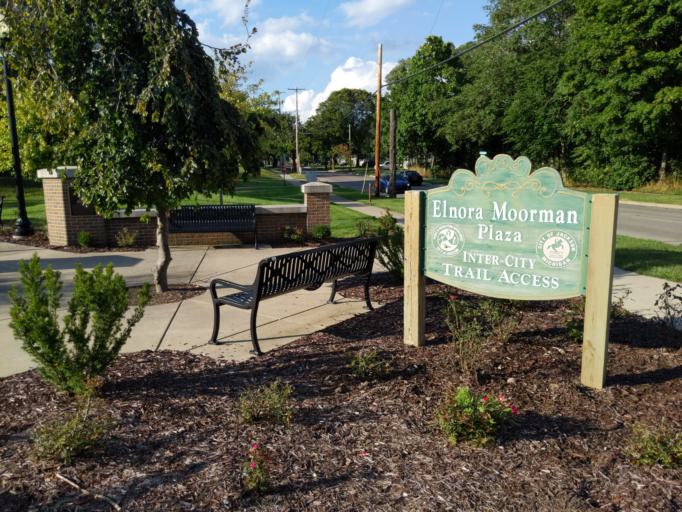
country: US
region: Michigan
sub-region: Jackson County
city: Jackson
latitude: 42.2330
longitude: -84.4004
